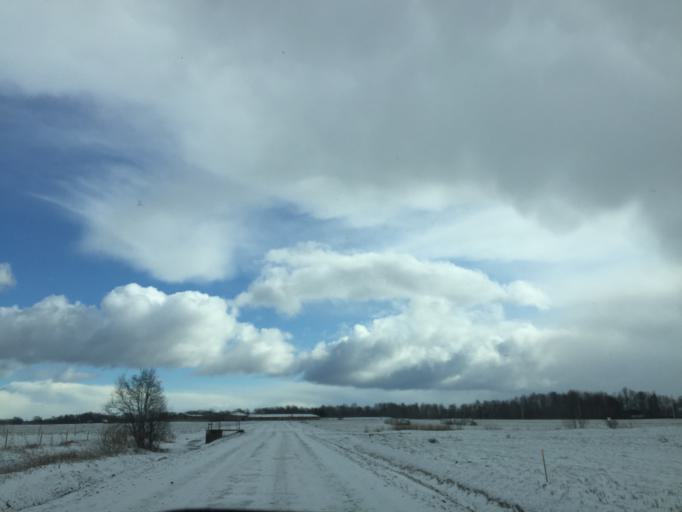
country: LV
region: Ventspils
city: Ventspils
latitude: 57.3729
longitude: 21.6241
